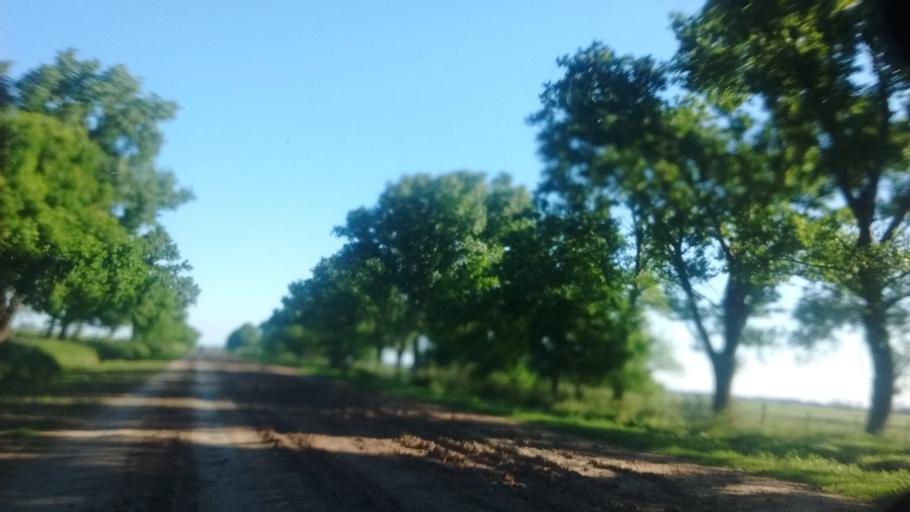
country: AR
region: Santa Fe
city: Funes
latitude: -32.8740
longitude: -60.7985
